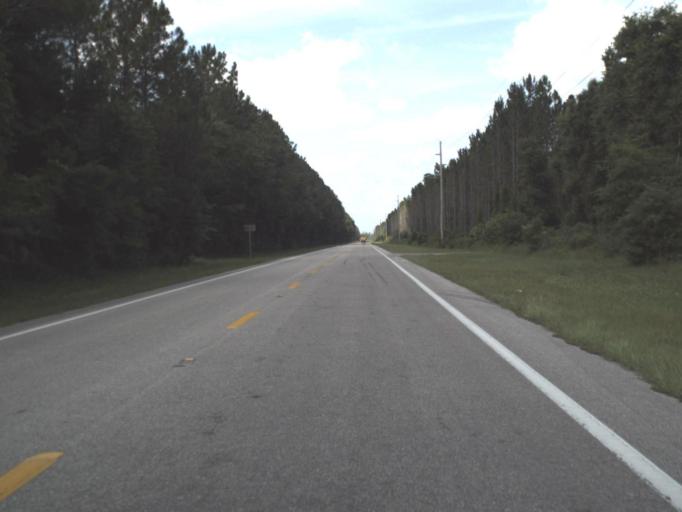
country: US
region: Florida
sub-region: Levy County
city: Bronson
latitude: 29.4357
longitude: -82.6553
